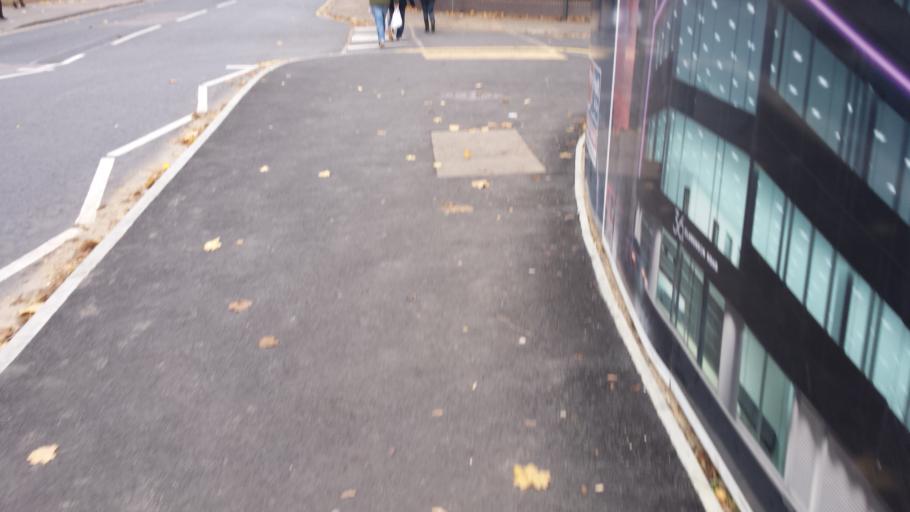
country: GB
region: England
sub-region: Hertfordshire
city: Watford
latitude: 51.6589
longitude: -0.3969
